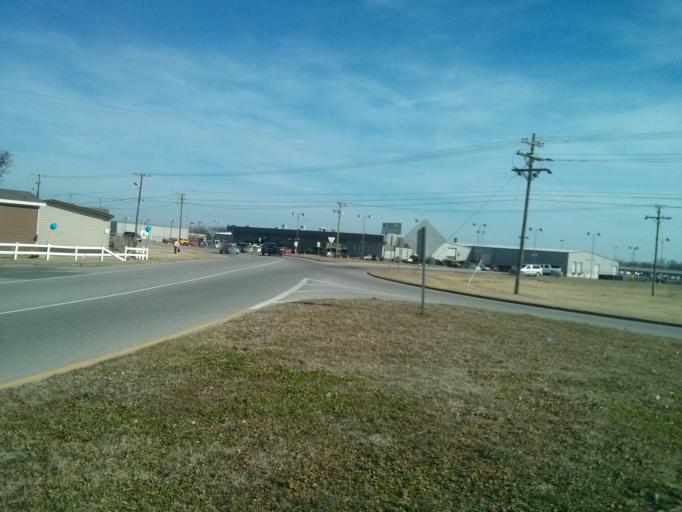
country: US
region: Oklahoma
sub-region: Tulsa County
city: Owasso
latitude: 36.1607
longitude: -95.8695
